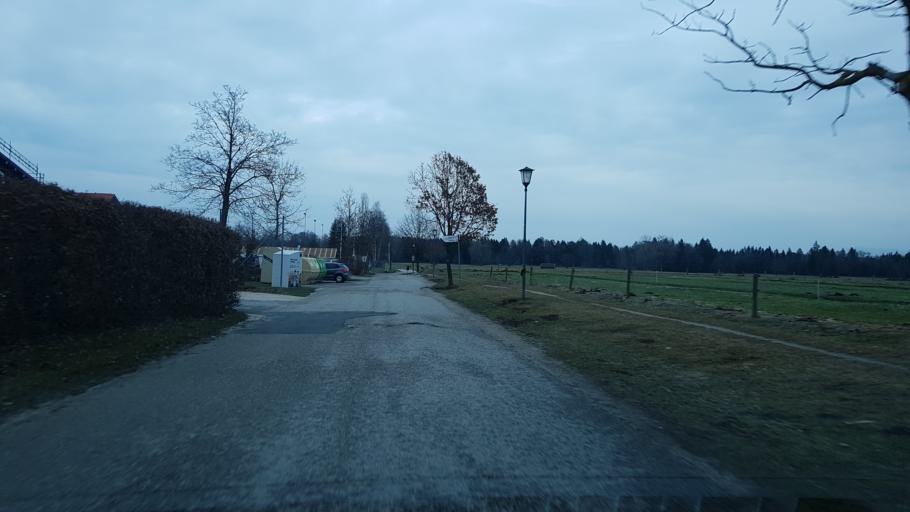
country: DE
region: Bavaria
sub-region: Upper Bavaria
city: Bernau am Chiemsee
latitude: 47.8093
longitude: 12.3825
